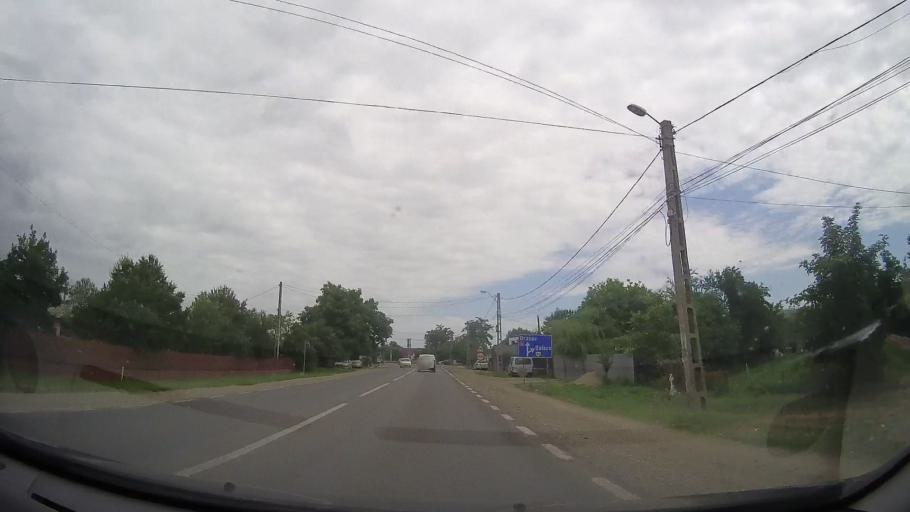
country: RO
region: Prahova
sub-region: Comuna Blejoiu
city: Blejoi
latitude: 45.0020
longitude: 26.0185
